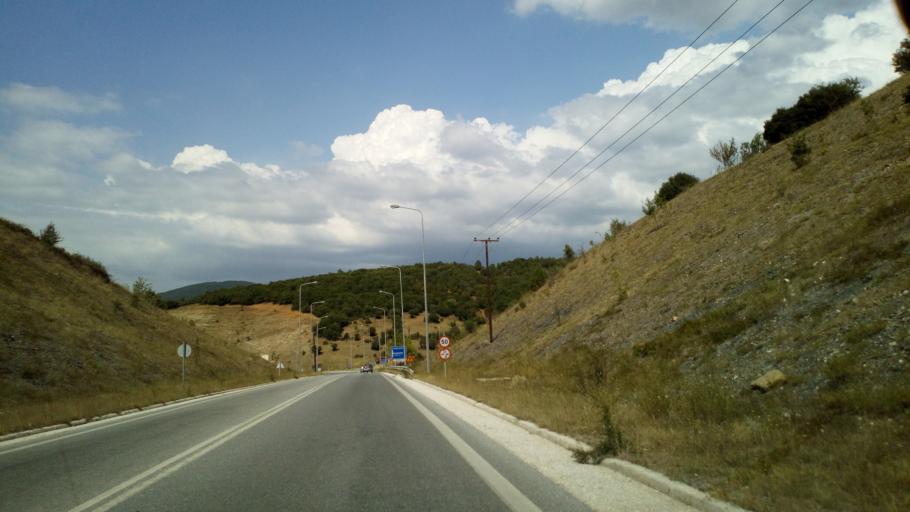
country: GR
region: Central Macedonia
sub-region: Nomos Chalkidikis
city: Polygyros
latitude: 40.4396
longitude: 23.4214
